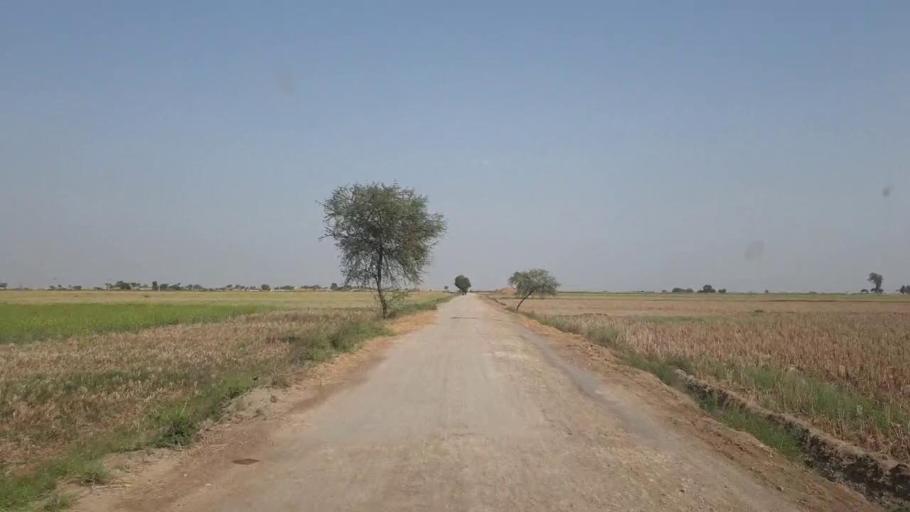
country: PK
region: Sindh
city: Kario
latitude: 24.5356
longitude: 68.5387
